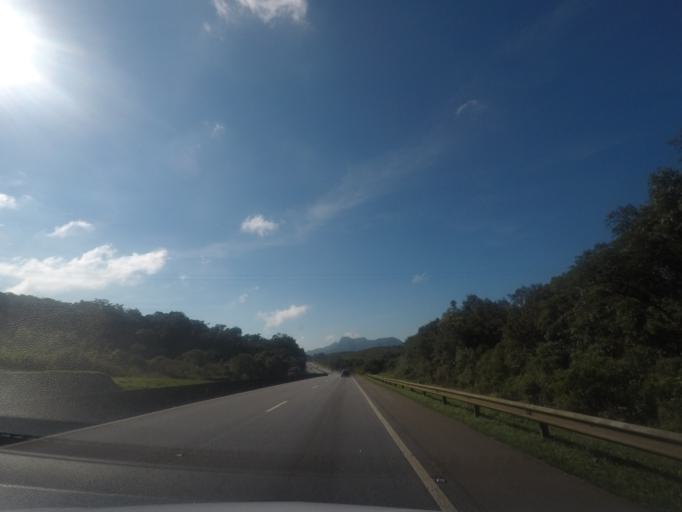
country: BR
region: Parana
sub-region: Piraquara
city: Piraquara
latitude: -25.5879
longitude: -48.9477
